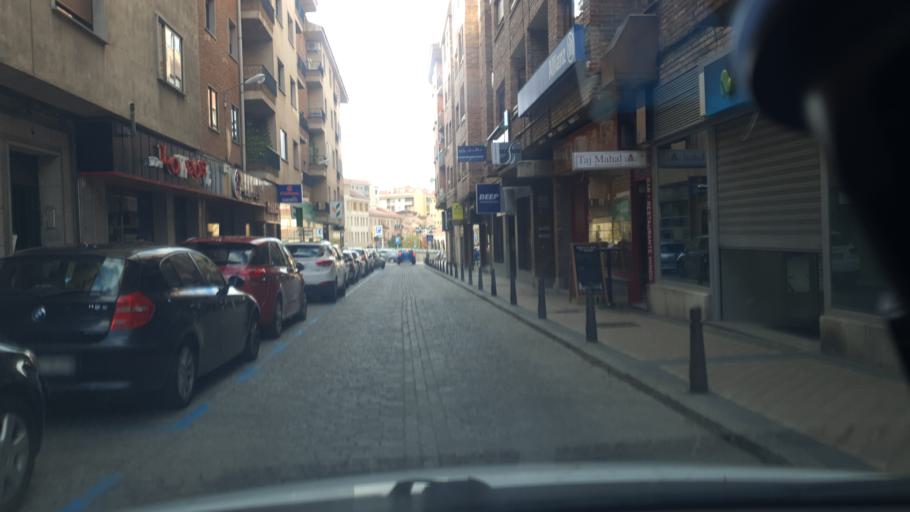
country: ES
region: Castille and Leon
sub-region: Provincia de Segovia
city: Segovia
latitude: 40.9448
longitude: -4.1190
